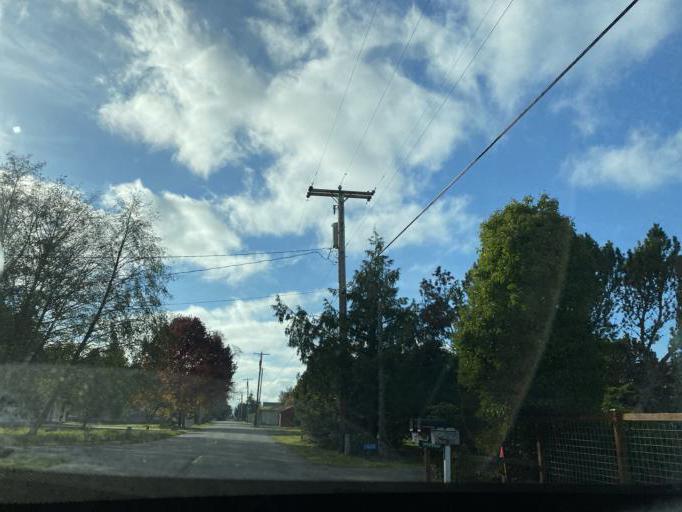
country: US
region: Washington
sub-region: Island County
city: Langley
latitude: 47.9404
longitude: -122.4418
